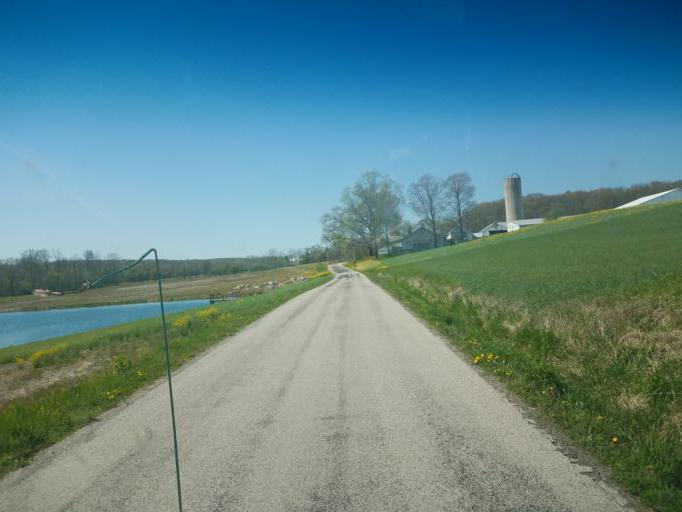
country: US
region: Ohio
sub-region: Medina County
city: Lodi
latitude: 40.9495
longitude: -82.0205
